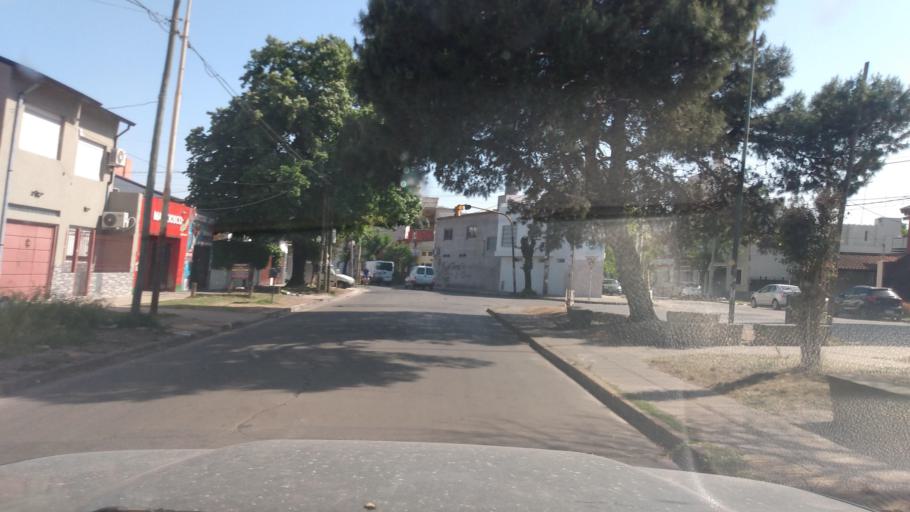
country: AR
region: Buenos Aires
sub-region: Partido de Moron
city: Moron
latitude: -34.6374
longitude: -58.5963
